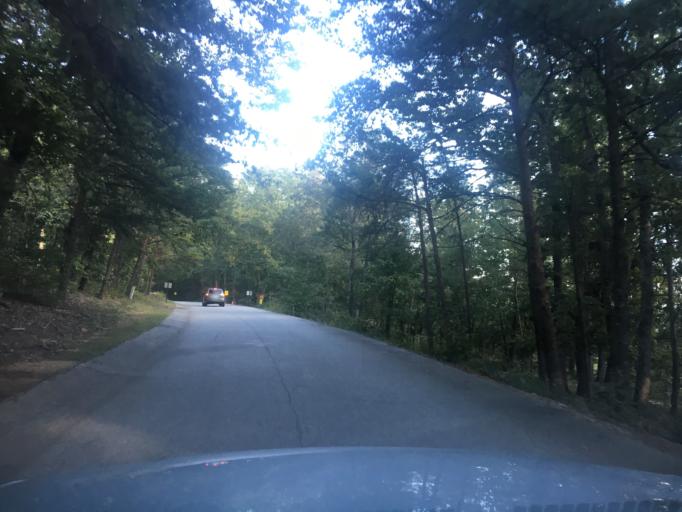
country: US
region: South Carolina
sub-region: Greenville County
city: Mauldin
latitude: 34.8390
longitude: -82.3097
